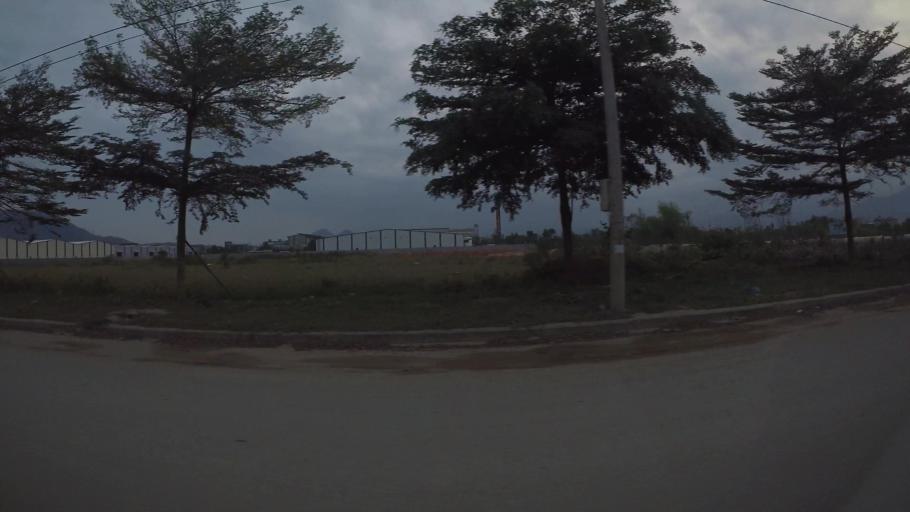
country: VN
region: Da Nang
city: Lien Chieu
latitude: 16.0903
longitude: 108.1086
